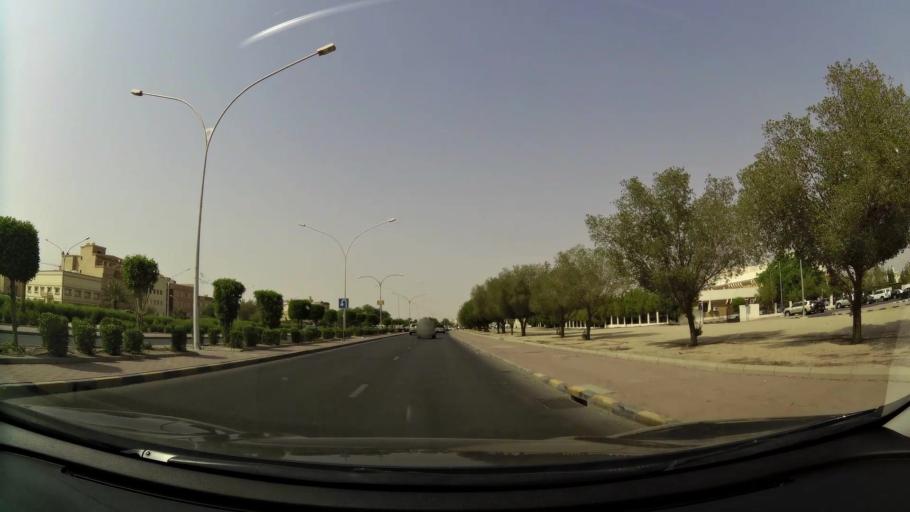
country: KW
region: Muhafazat al Jahra'
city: Al Jahra'
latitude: 29.3385
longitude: 47.6930
